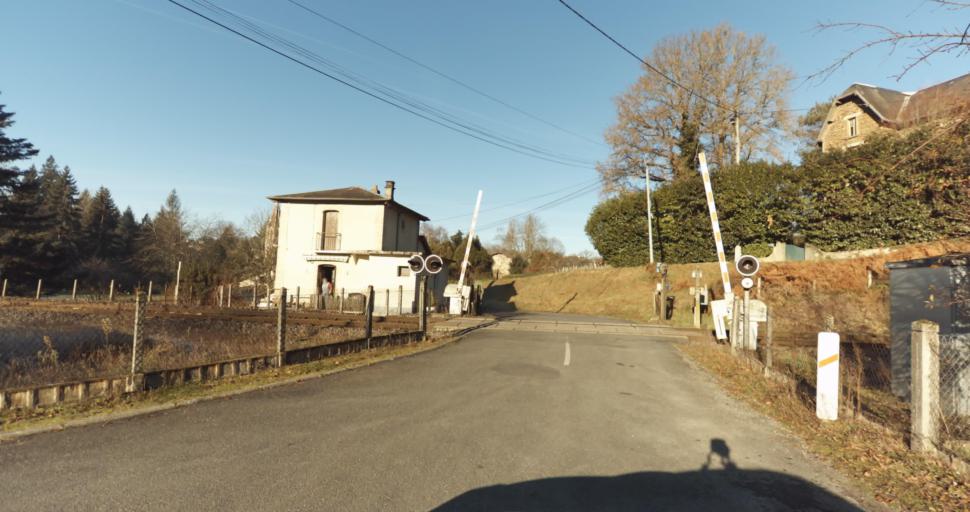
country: FR
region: Limousin
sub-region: Departement de la Haute-Vienne
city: Aixe-sur-Vienne
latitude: 45.7992
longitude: 1.1561
